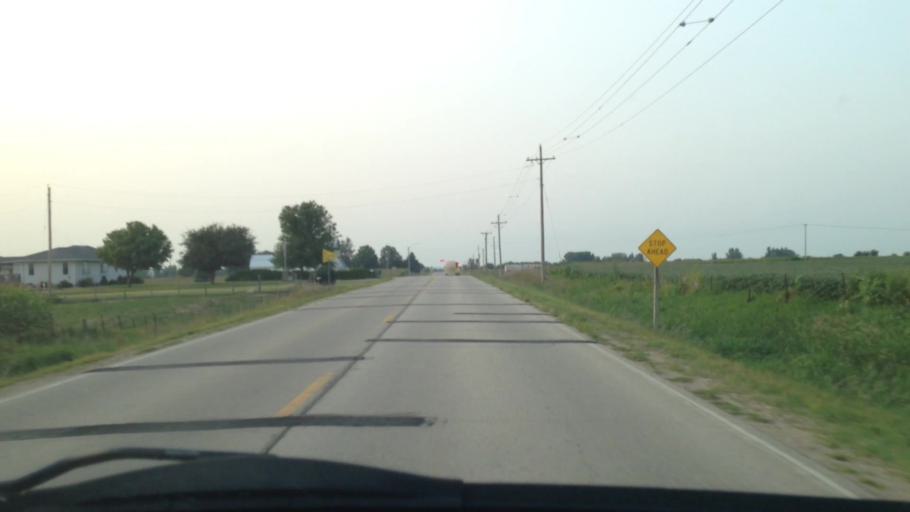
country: US
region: Iowa
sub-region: Benton County
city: Atkins
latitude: 41.9902
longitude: -91.8732
